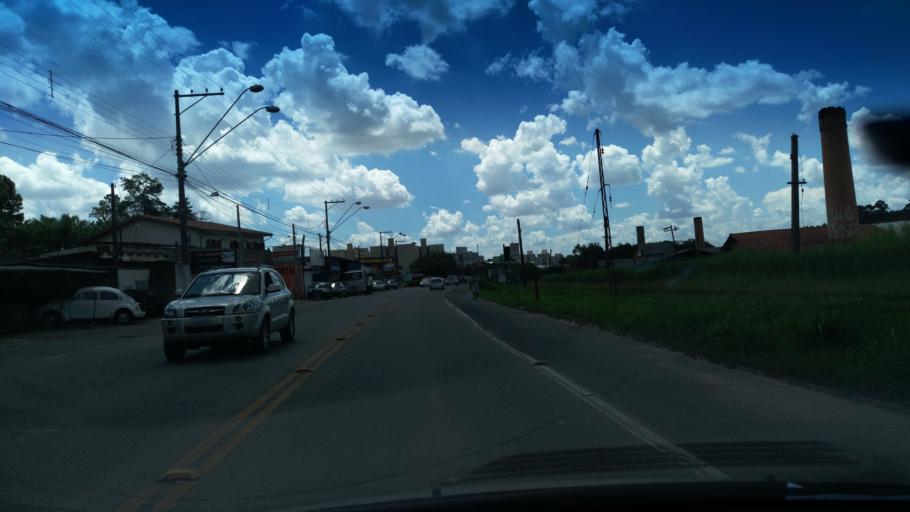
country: BR
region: Sao Paulo
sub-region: Vinhedo
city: Vinhedo
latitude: -23.0047
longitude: -46.9875
